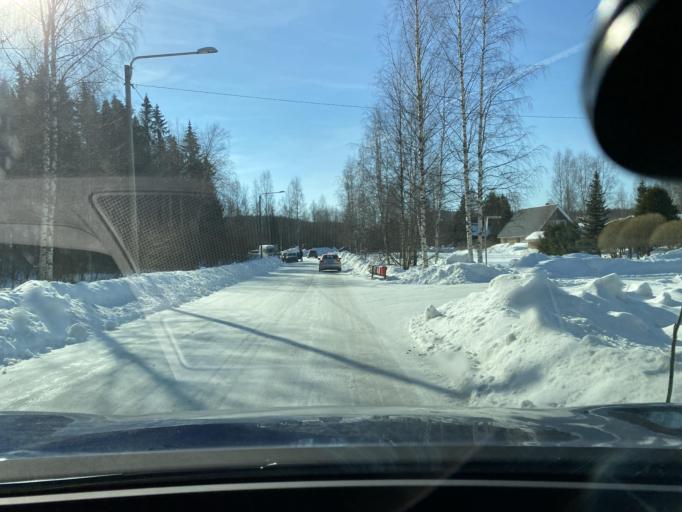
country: FI
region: Central Finland
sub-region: Jyvaeskylae
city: Muurame
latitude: 62.0939
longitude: 25.6434
